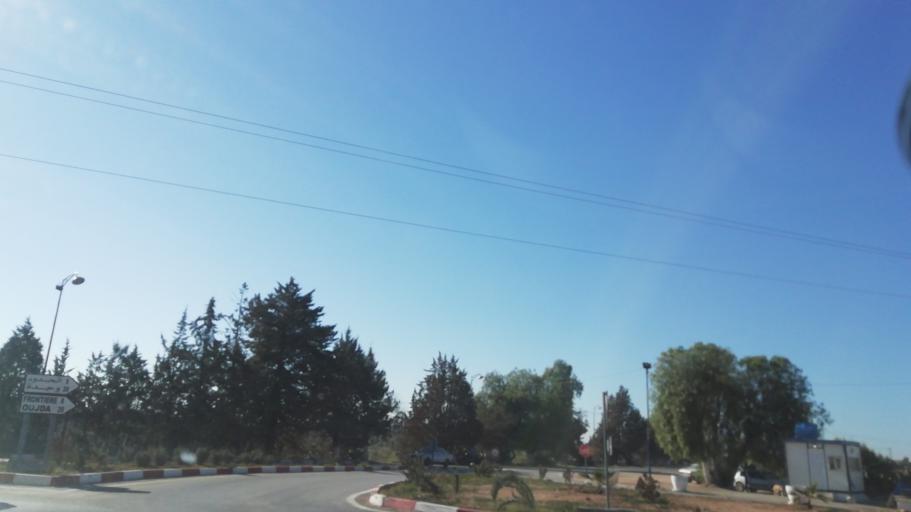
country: DZ
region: Tlemcen
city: Nedroma
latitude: 34.8378
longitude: -1.7801
